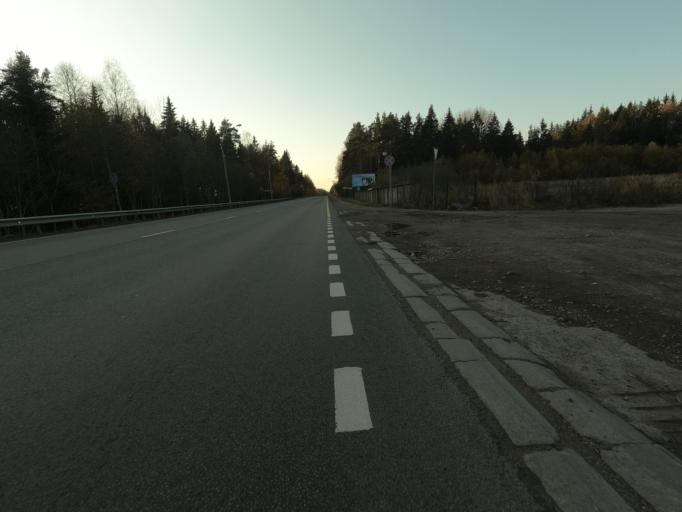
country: RU
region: St.-Petersburg
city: Pesochnyy
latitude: 60.1788
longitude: 30.1453
